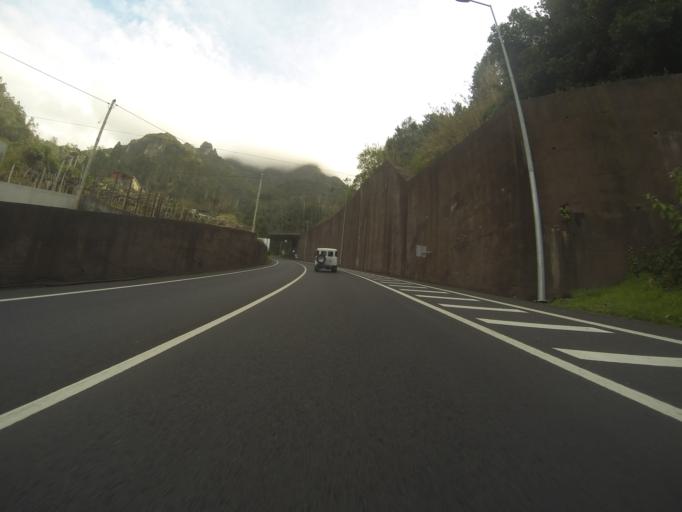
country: PT
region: Madeira
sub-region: Sao Vicente
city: Sao Vicente
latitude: 32.7691
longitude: -17.0307
